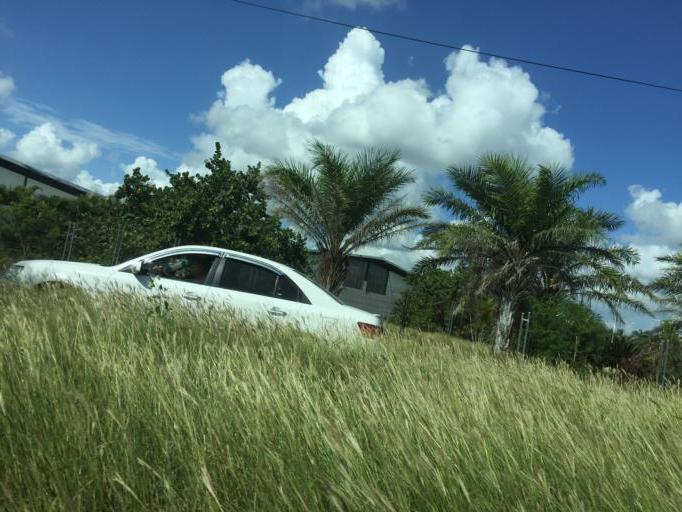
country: DO
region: Santo Domingo
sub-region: Santo Domingo
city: Boca Chica
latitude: 18.4593
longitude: -69.6608
